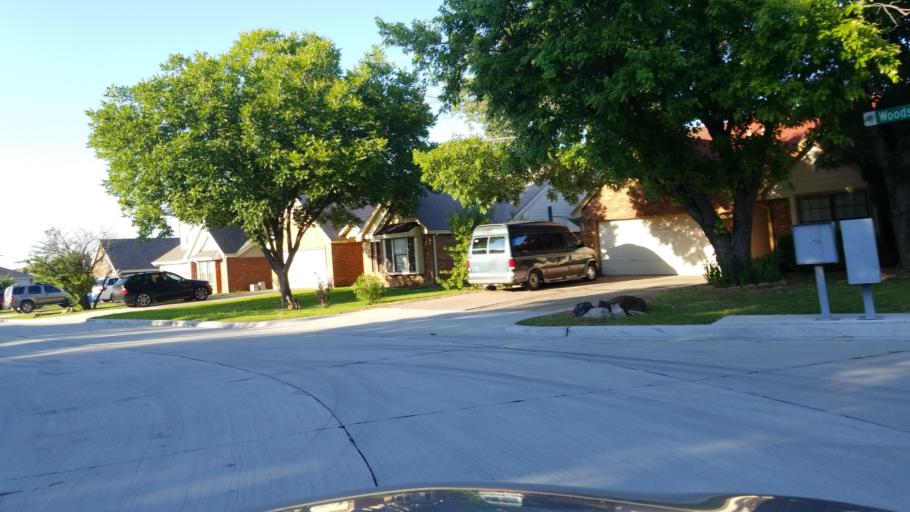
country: US
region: Texas
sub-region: Dallas County
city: Grand Prairie
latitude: 32.6919
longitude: -97.0353
